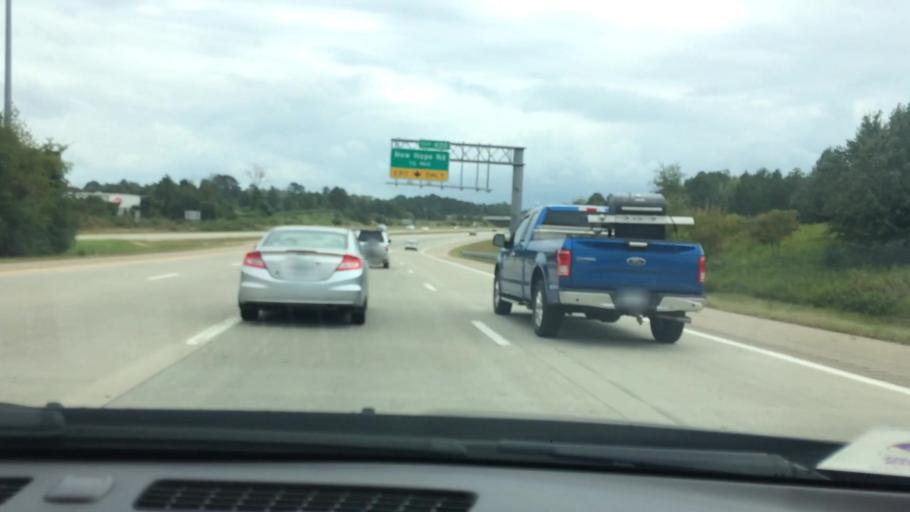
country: US
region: North Carolina
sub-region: Wake County
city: Raleigh
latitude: 35.7798
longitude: -78.5682
